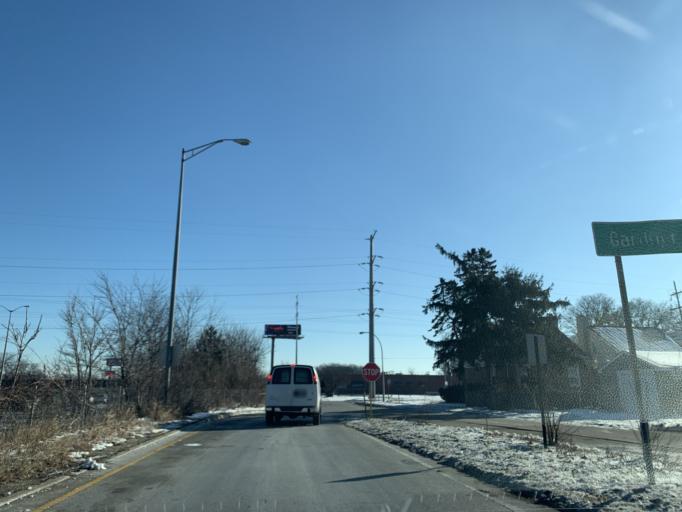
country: US
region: Illinois
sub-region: Cook County
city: Broadview
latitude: 41.8707
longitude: -87.8690
